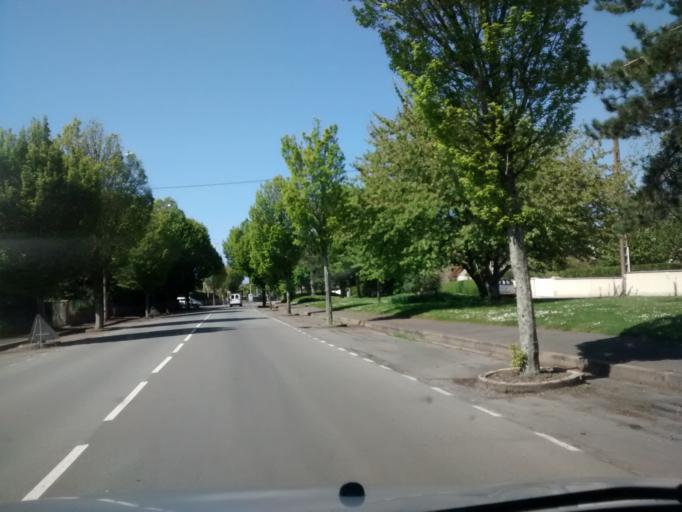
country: FR
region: Brittany
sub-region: Departement d'Ille-et-Vilaine
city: Dinard
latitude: 48.6281
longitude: -2.0743
